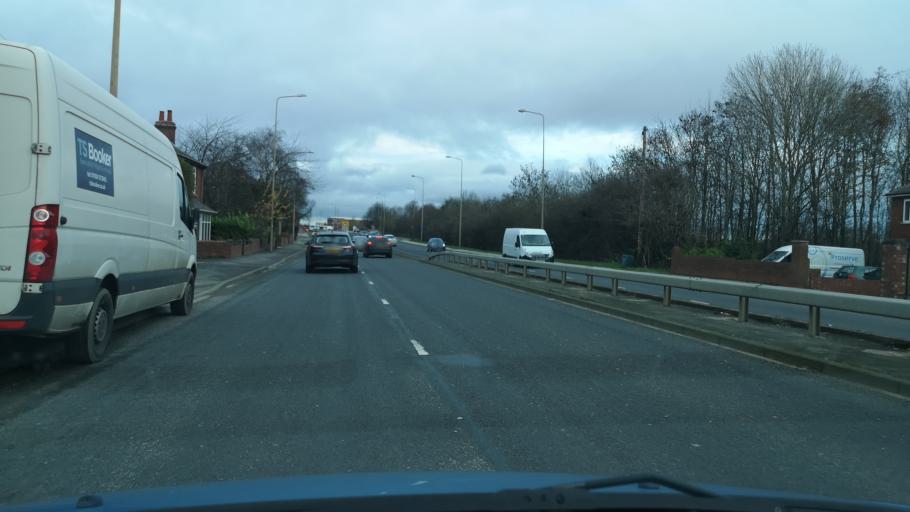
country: GB
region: England
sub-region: City and Borough of Wakefield
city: Wakefield
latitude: 53.6609
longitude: -1.5104
